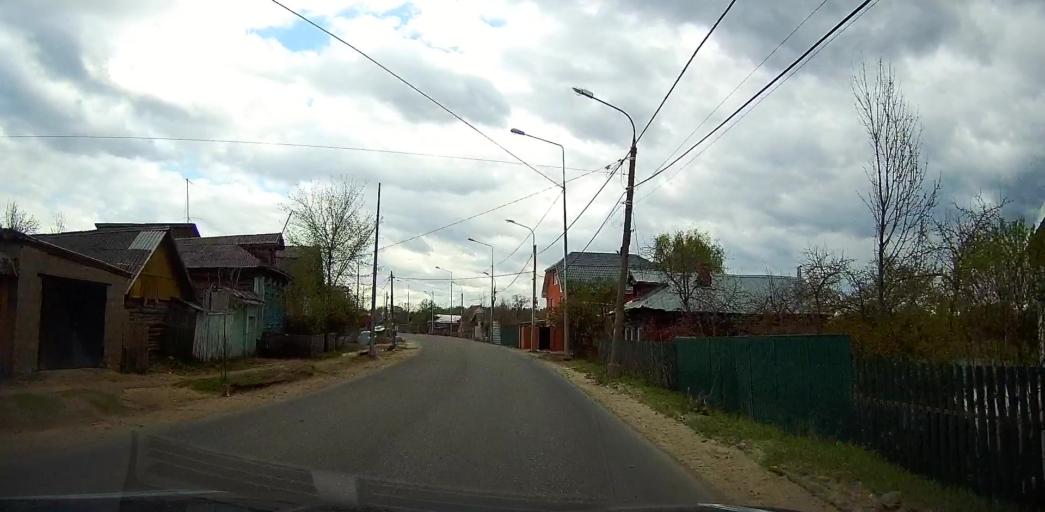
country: RU
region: Moskovskaya
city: Pavlovskiy Posad
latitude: 55.7915
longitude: 38.6851
